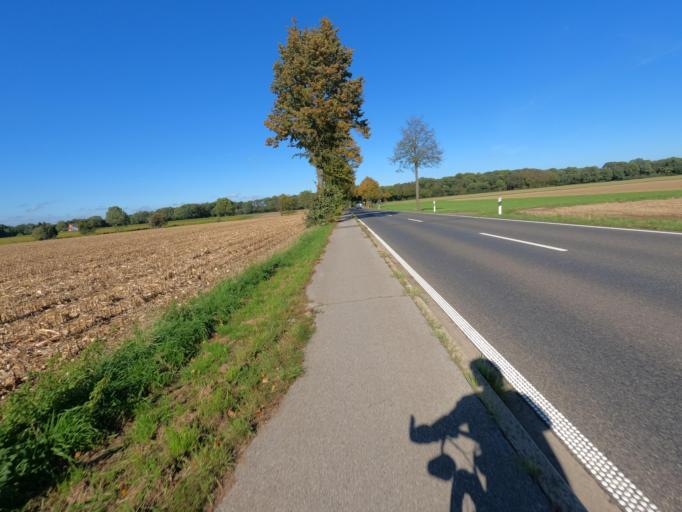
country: DE
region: North Rhine-Westphalia
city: Erkelenz
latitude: 51.0488
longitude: 6.3232
